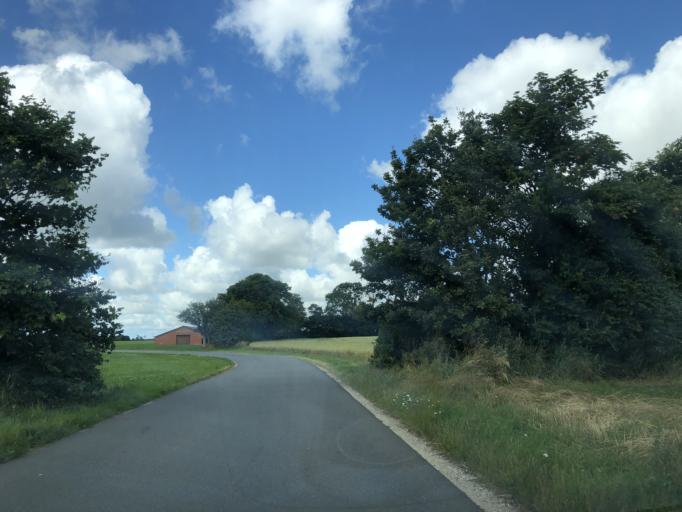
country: DK
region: Central Jutland
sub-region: Struer Kommune
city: Struer
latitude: 56.4779
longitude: 8.5372
